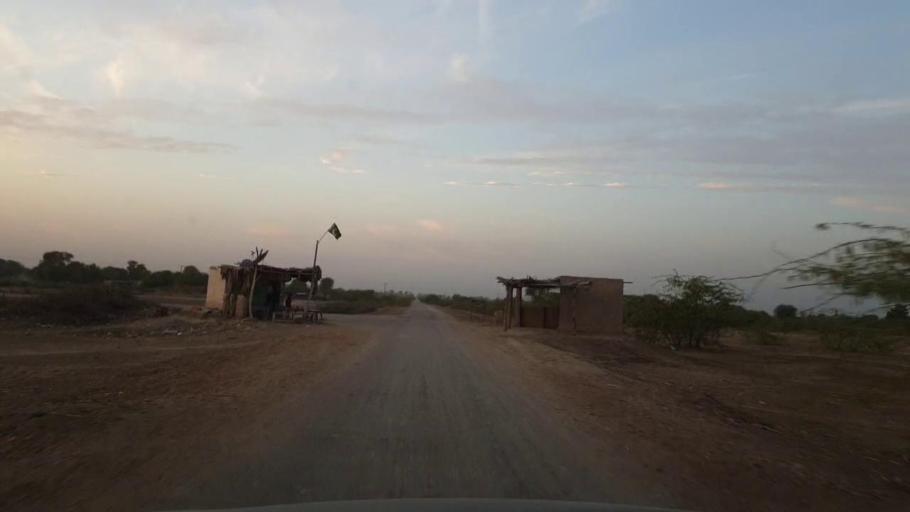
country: PK
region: Sindh
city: Kunri
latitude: 25.1321
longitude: 69.5649
